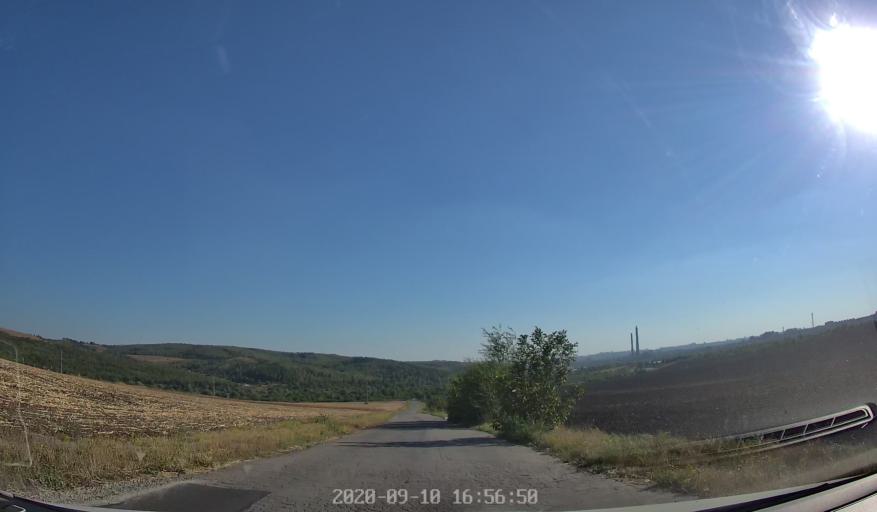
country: MD
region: Chisinau
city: Stauceni
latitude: 47.0537
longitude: 28.9166
